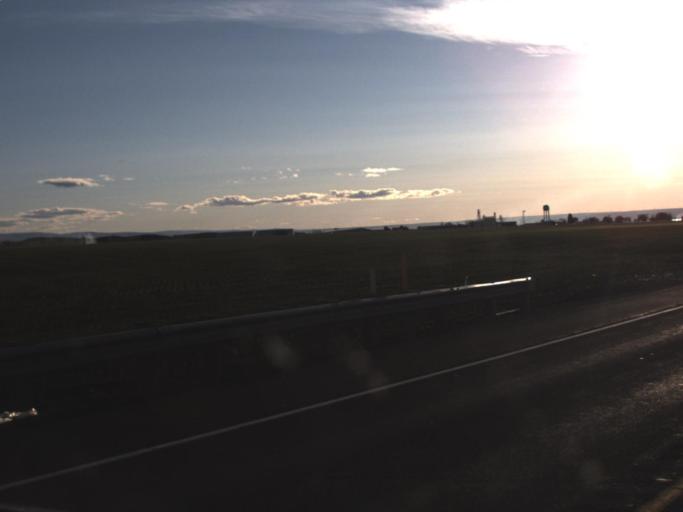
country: US
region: Washington
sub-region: Walla Walla County
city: Walla Walla East
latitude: 46.1012
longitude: -118.2486
